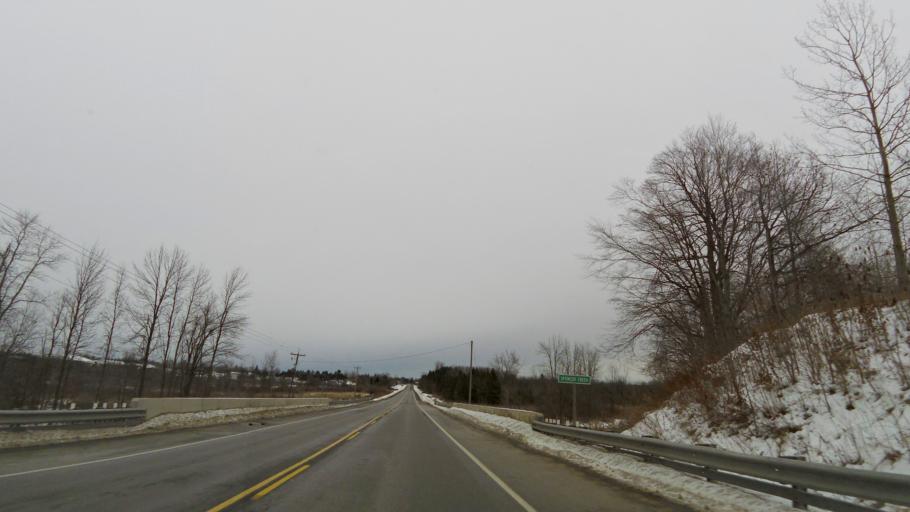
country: CA
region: Ontario
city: Ancaster
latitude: 43.2829
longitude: -80.0538
